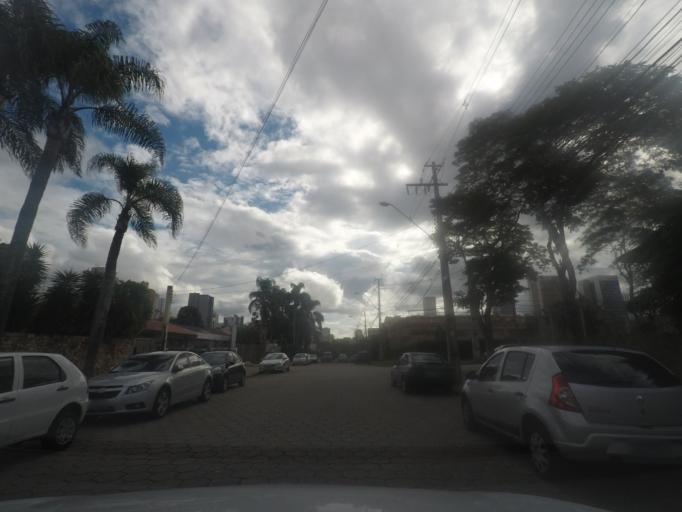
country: BR
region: Parana
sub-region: Curitiba
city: Curitiba
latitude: -25.4329
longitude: -49.2479
